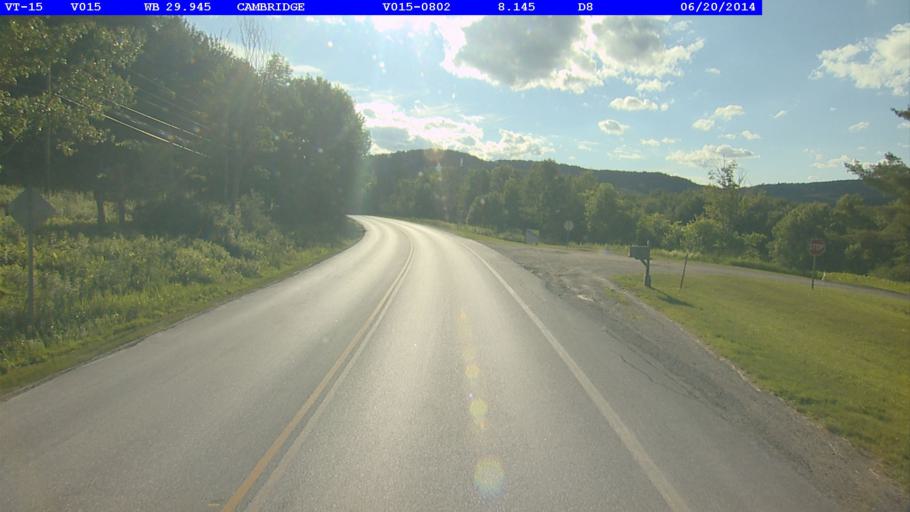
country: US
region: Vermont
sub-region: Lamoille County
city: Johnson
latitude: 44.6664
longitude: -72.7782
